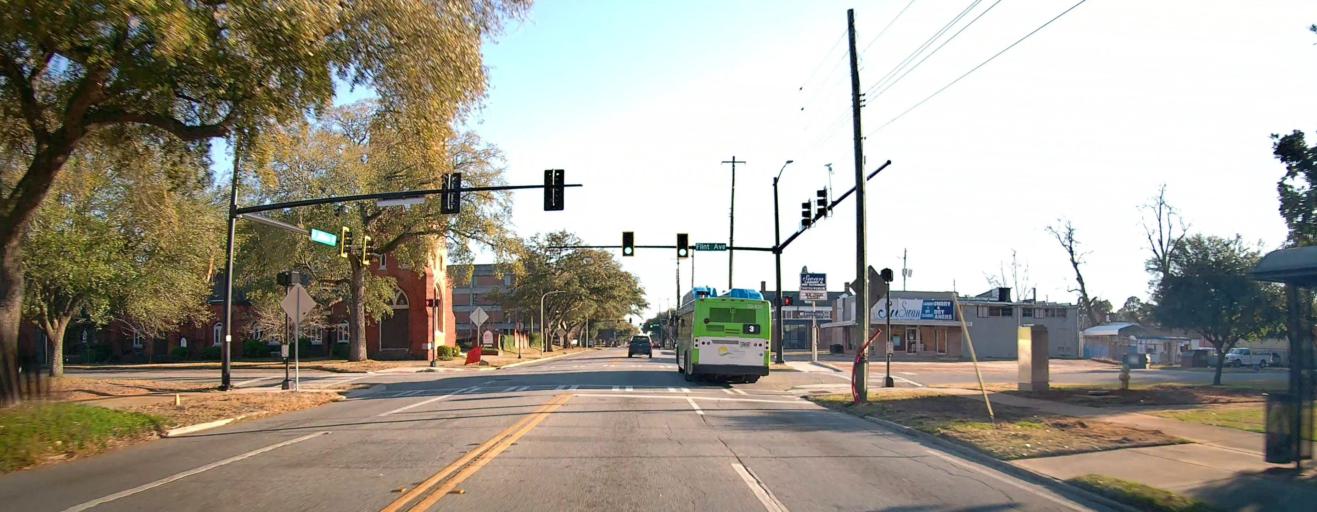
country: US
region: Georgia
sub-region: Dougherty County
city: Albany
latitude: 31.5803
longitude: -84.1560
